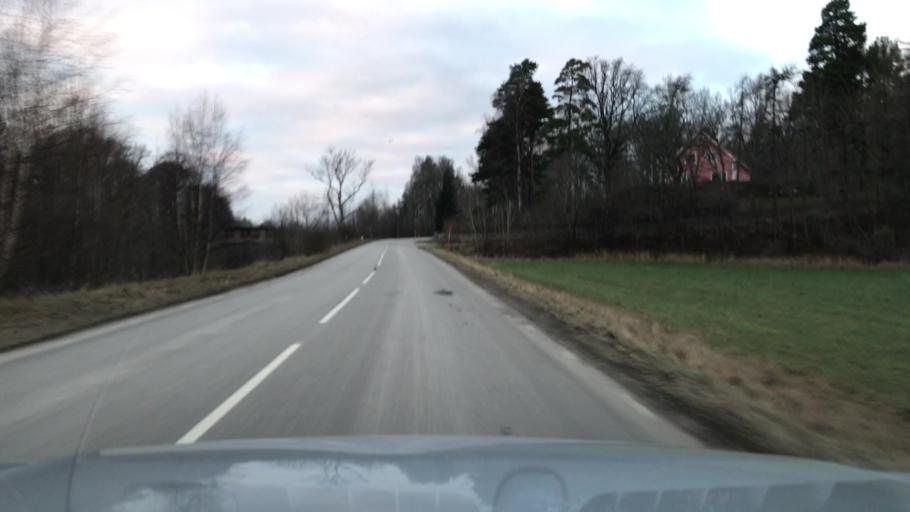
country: SE
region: OEstergoetland
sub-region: Norrkopings Kommun
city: Kimstad
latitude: 58.5153
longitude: 15.9752
